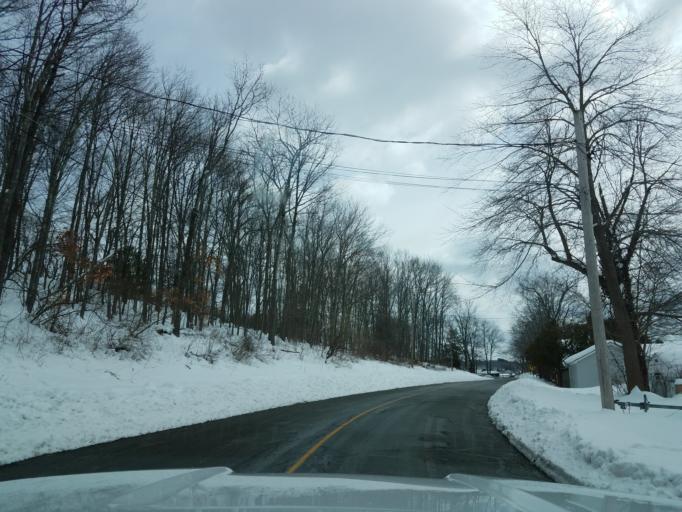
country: US
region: Connecticut
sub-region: Litchfield County
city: Litchfield
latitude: 41.7115
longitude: -73.2332
